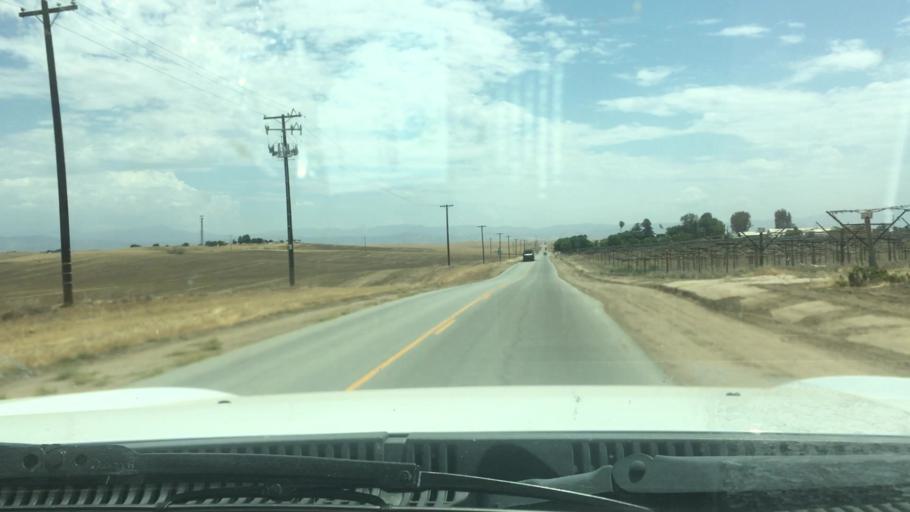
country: US
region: California
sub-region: Kern County
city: McFarland
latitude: 35.6025
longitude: -119.0966
